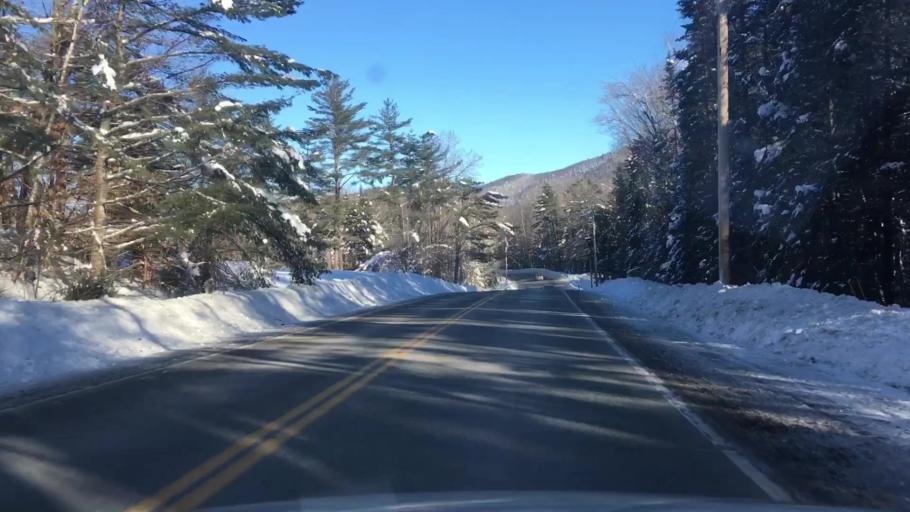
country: US
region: Maine
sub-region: Oxford County
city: West Paris
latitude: 44.3987
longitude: -70.6342
